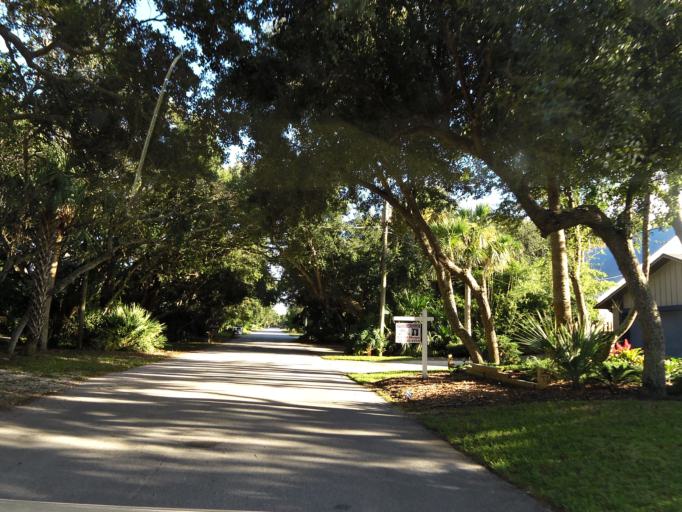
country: US
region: Florida
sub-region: Flagler County
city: Flagler Beach
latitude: 29.4585
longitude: -81.1203
